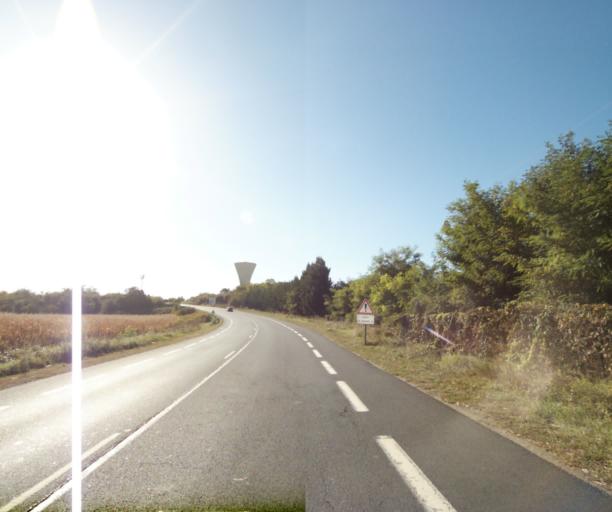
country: FR
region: Auvergne
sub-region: Departement du Puy-de-Dome
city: Gerzat
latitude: 45.8429
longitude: 3.1420
